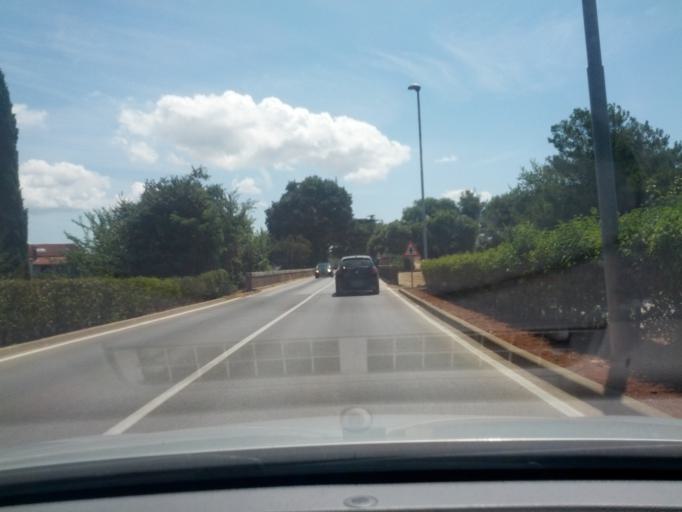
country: HR
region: Istarska
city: Fazana
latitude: 44.9155
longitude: 13.8154
